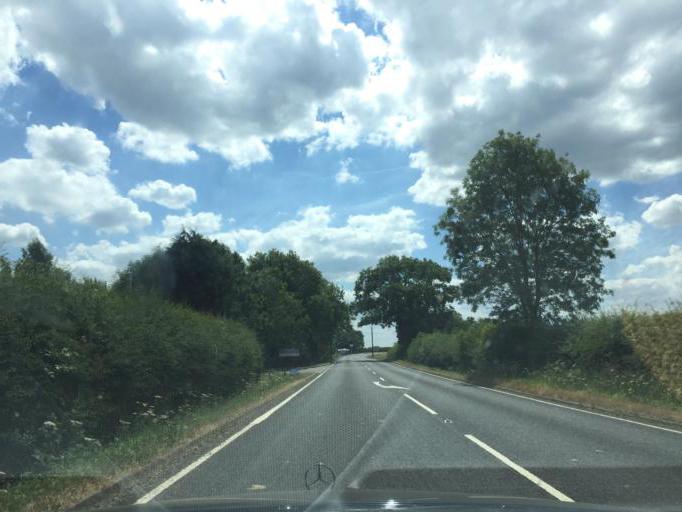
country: GB
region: England
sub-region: Leicestershire
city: Hinckley
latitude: 52.4751
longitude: -1.3761
